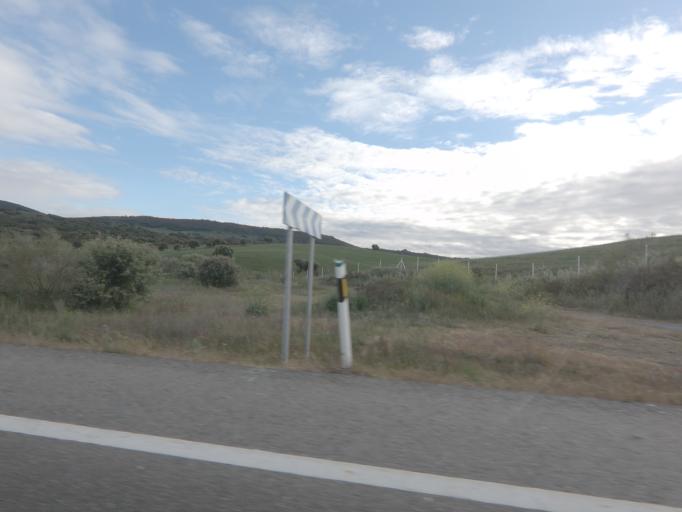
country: ES
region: Extremadura
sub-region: Provincia de Caceres
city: Pedroso de Acim
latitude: 39.8346
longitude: -6.3908
